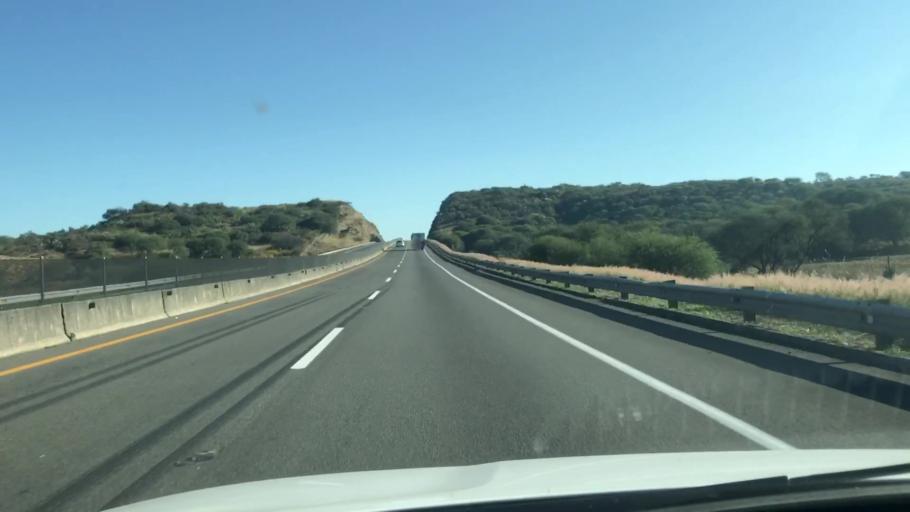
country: MX
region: Jalisco
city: Jalostotitlan
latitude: 21.1356
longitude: -102.4396
